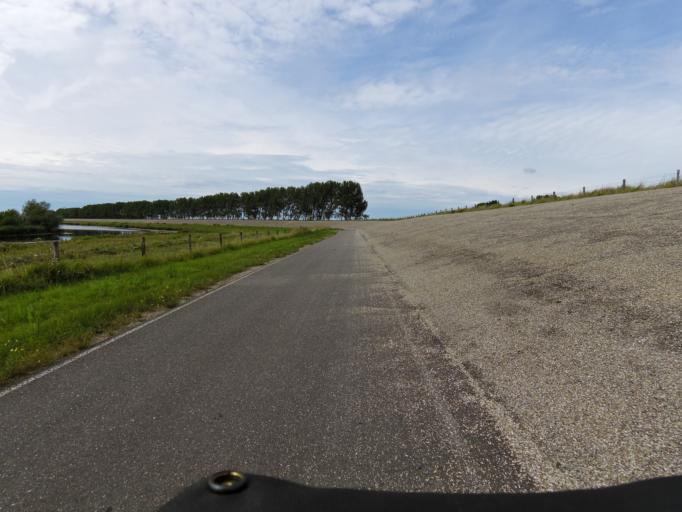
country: NL
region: South Holland
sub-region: Gemeente Goeree-Overflakkee
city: Middelharnis
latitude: 51.6822
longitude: 4.1915
